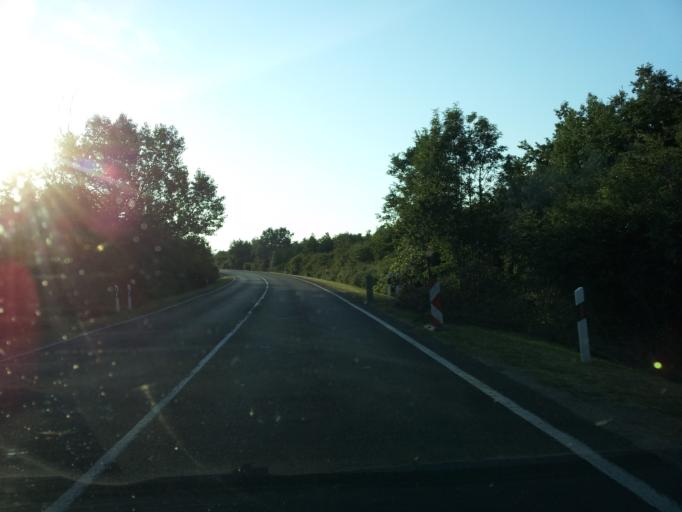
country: HU
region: Fejer
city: Szarliget
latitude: 47.4905
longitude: 18.5235
